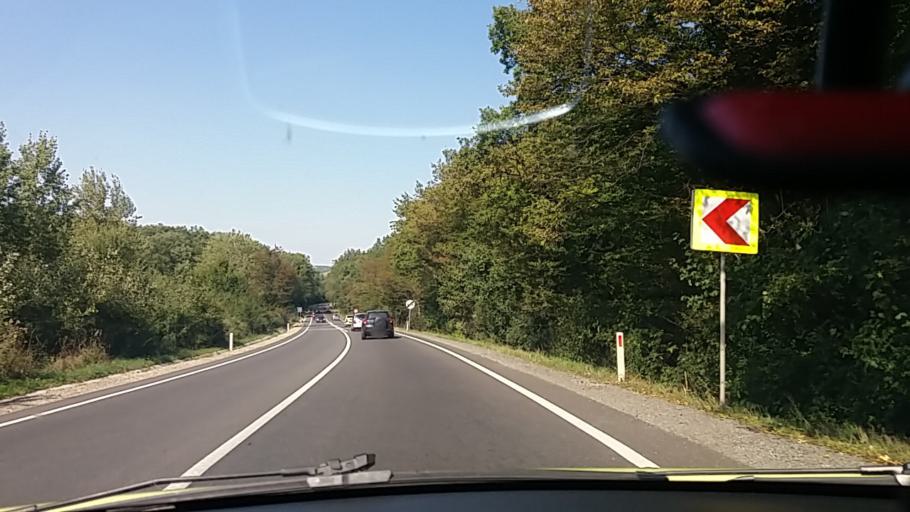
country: RO
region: Sibiu
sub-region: Comuna Sura Mare
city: Sura Mare
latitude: 45.8820
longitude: 24.1640
